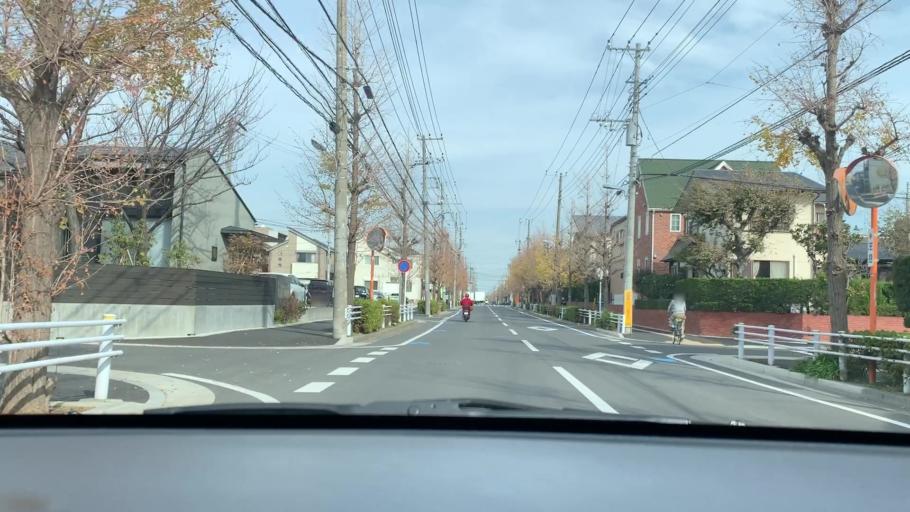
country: JP
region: Tokyo
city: Urayasu
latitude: 35.6417
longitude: 139.8976
